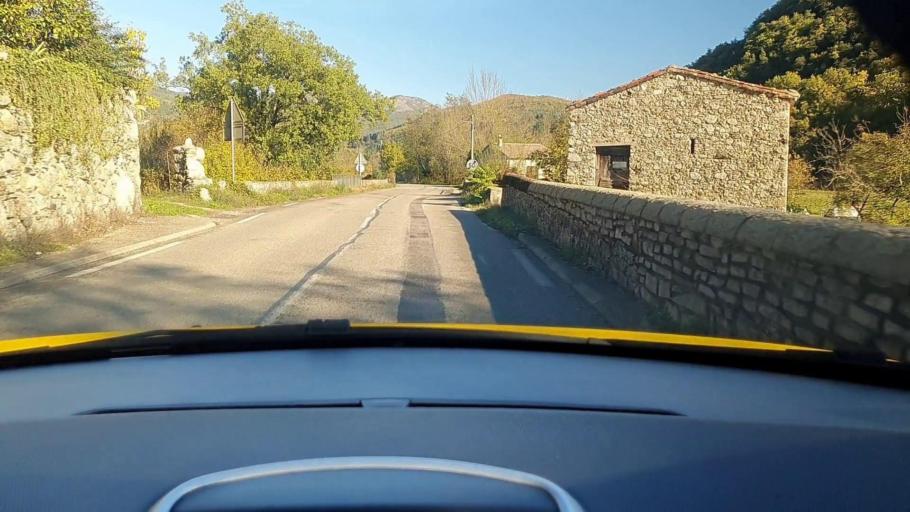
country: FR
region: Languedoc-Roussillon
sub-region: Departement du Gard
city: Le Vigan
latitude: 43.9829
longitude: 3.5837
